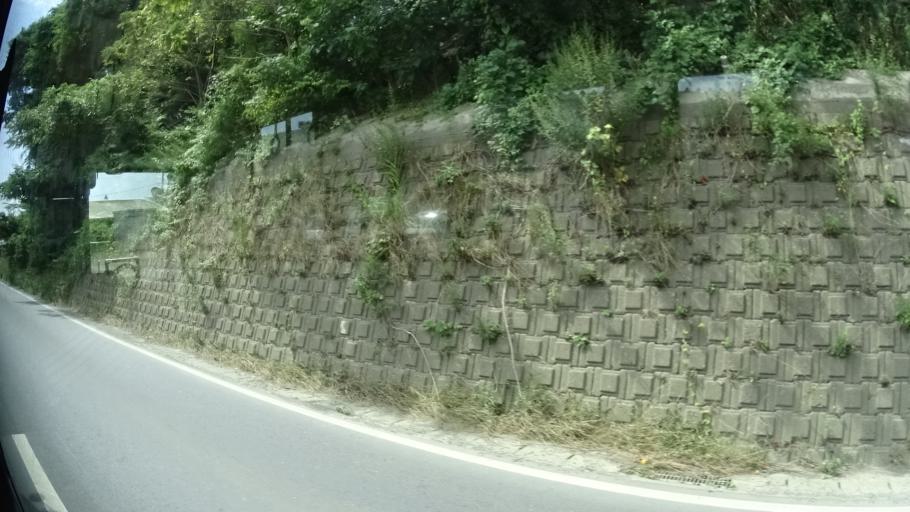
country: JP
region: Iwate
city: Ofunato
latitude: 38.8780
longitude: 141.5781
